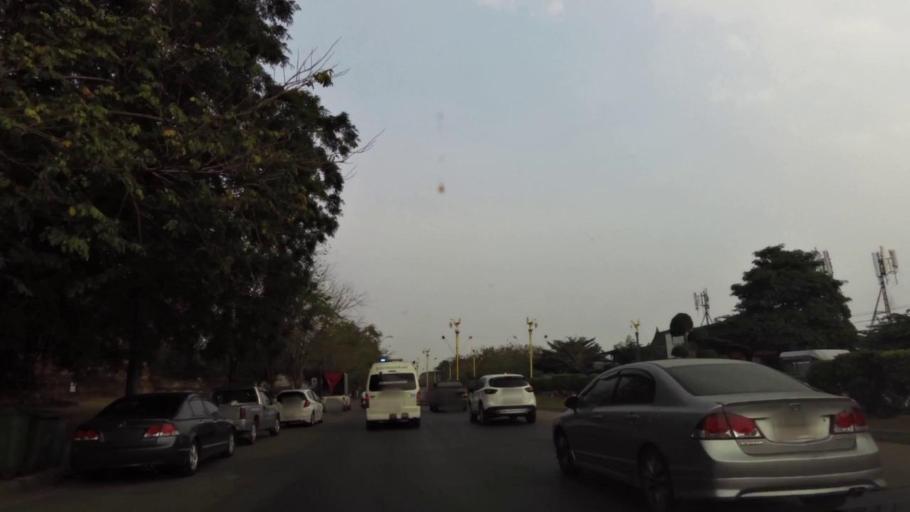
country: TH
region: Phra Nakhon Si Ayutthaya
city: Phra Nakhon Si Ayutthaya
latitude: 14.3511
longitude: 100.5661
